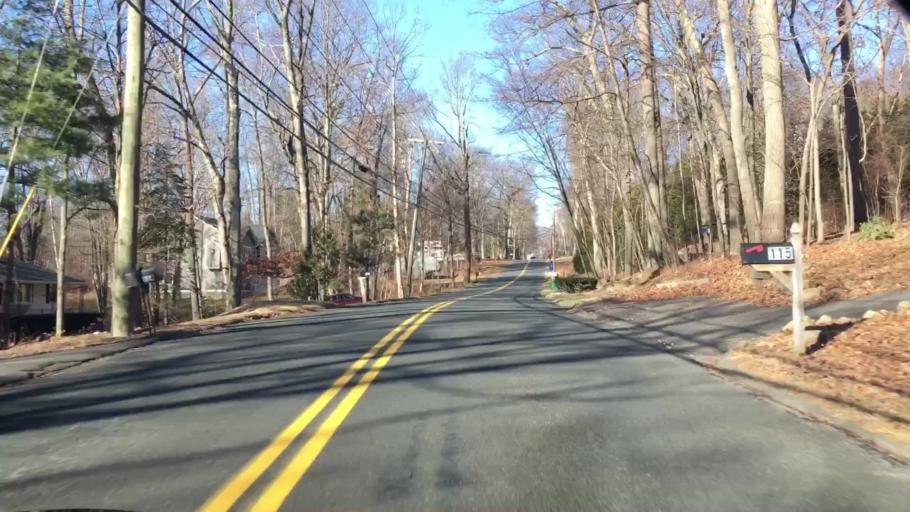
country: US
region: Connecticut
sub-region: Tolland County
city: Crystal Lake
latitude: 41.9391
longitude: -72.3901
